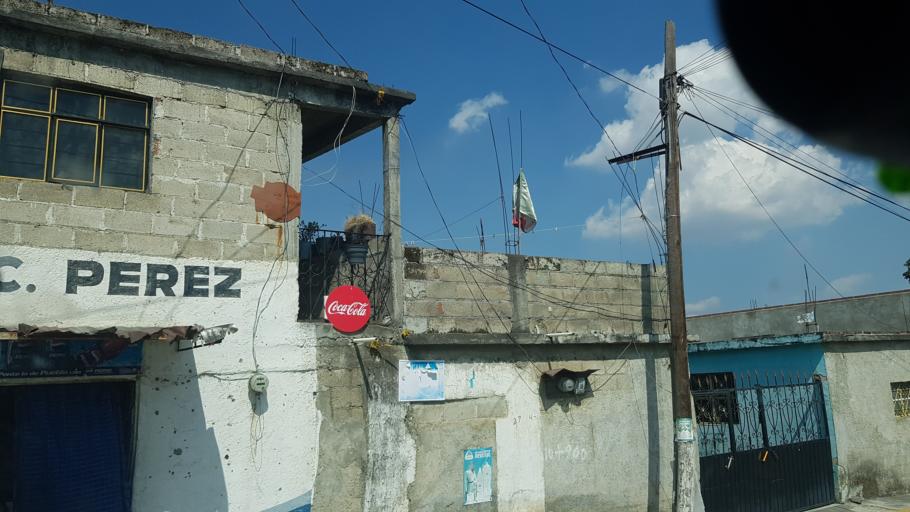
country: MX
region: Puebla
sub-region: Atlixco
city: San Pedro Benito Juarez
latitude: 18.9486
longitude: -98.5491
